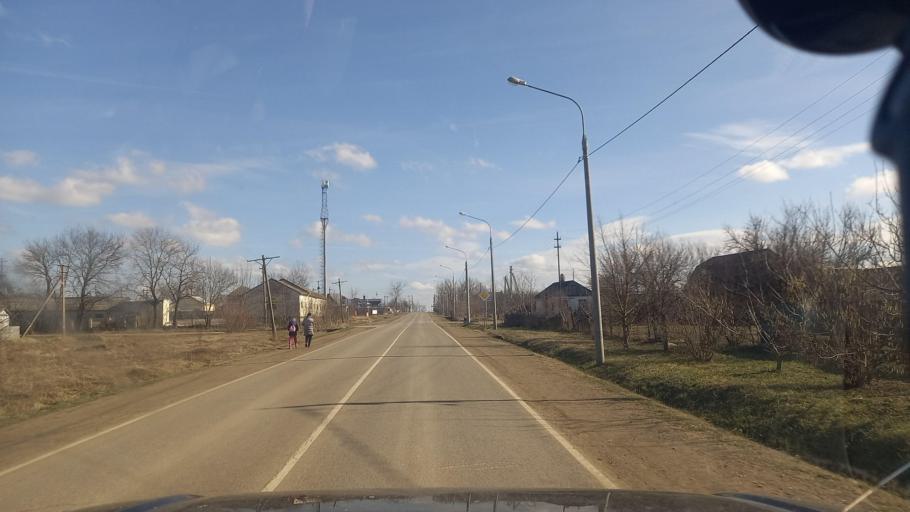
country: RU
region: Krasnodarskiy
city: Novodmitriyevskaya
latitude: 44.8275
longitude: 38.8905
